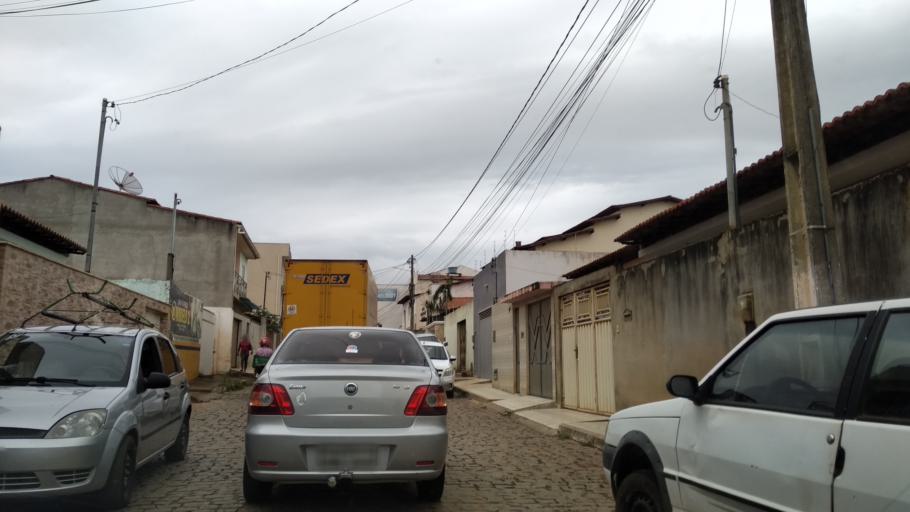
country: BR
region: Bahia
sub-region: Caetite
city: Caetite
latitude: -14.0670
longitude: -42.4808
